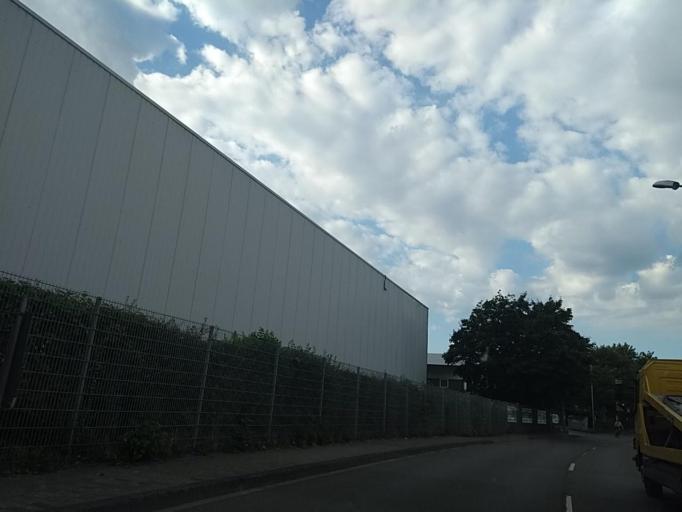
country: DE
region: North Rhine-Westphalia
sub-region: Regierungsbezirk Arnsberg
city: Brilon
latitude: 51.3999
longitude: 8.5850
